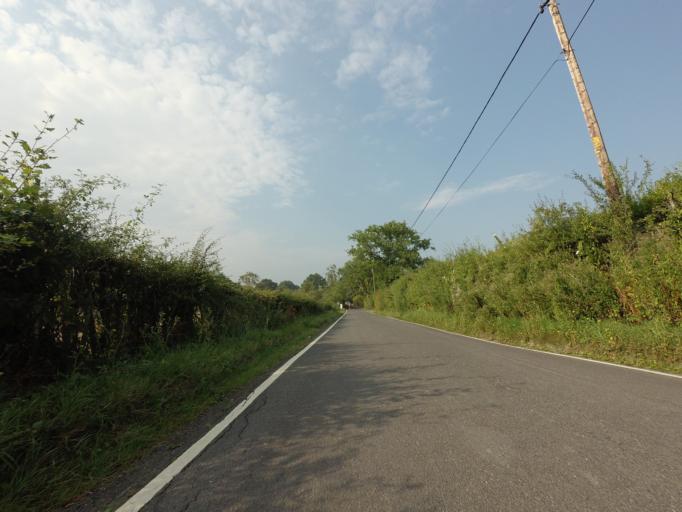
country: GB
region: England
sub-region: Kent
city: Tenterden
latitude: 51.1174
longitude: 0.6875
